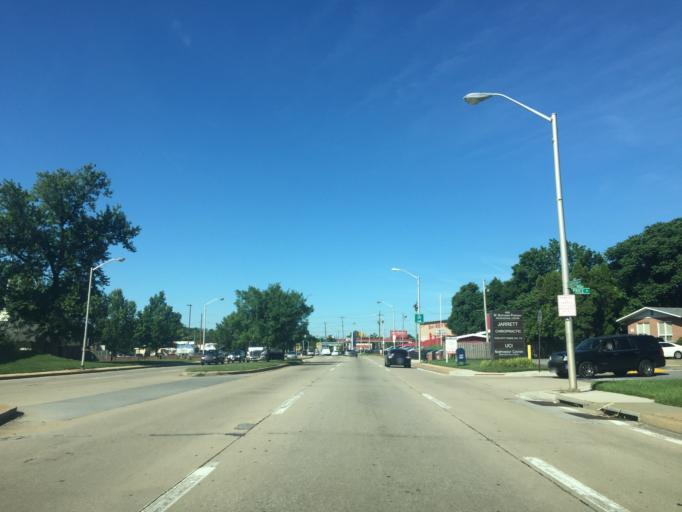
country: US
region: Maryland
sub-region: Baltimore County
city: Lochearn
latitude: 39.3498
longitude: -76.6900
